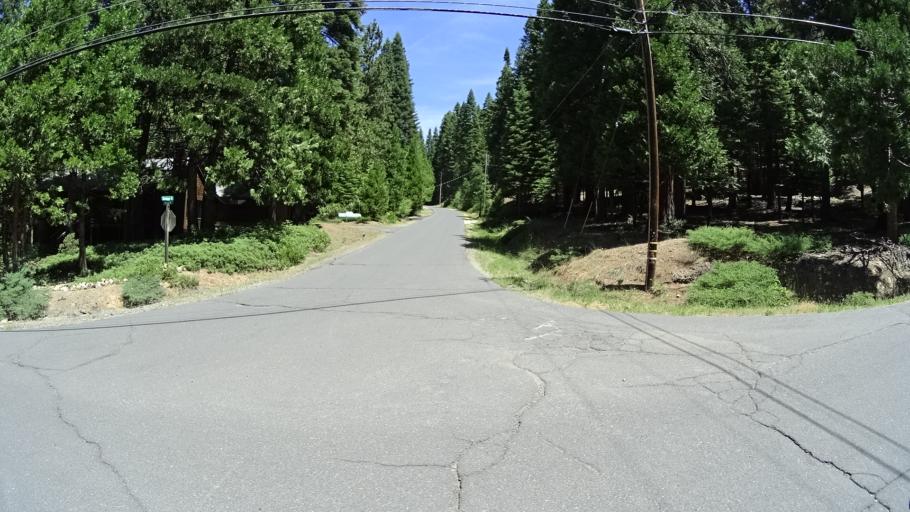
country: US
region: California
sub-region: Calaveras County
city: Arnold
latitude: 38.3122
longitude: -120.2623
